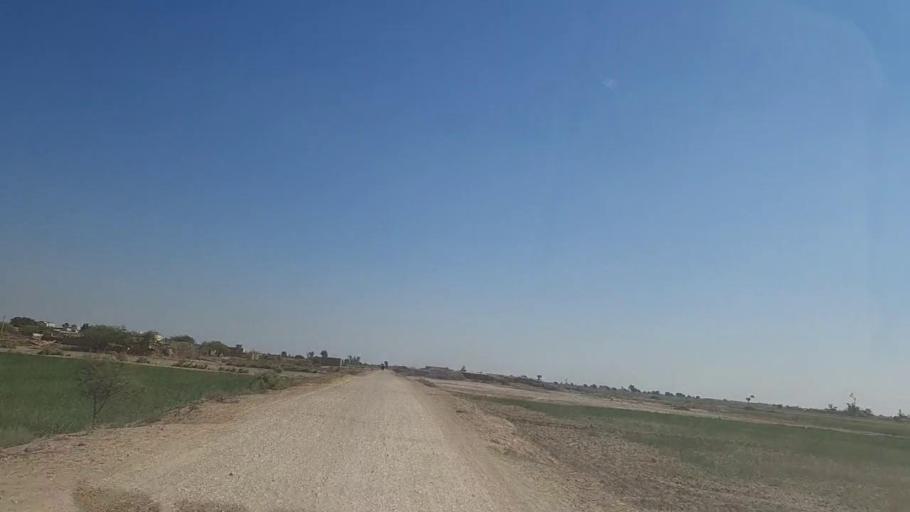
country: PK
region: Sindh
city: Digri
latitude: 25.1170
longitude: 69.1111
